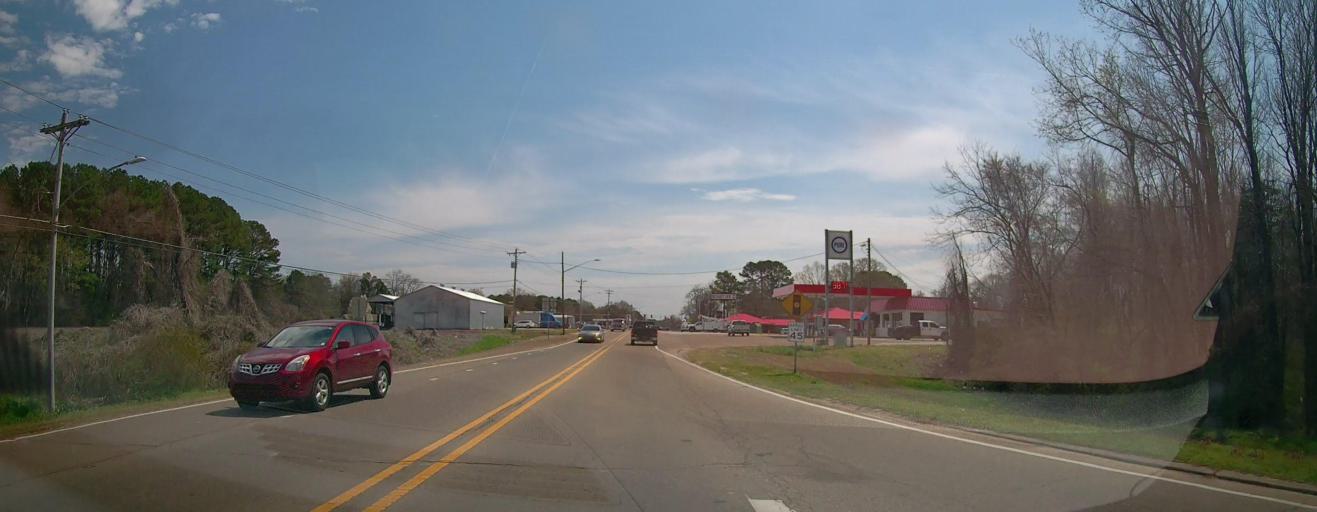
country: US
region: Mississippi
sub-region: Union County
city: New Albany
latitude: 34.5113
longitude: -89.0371
